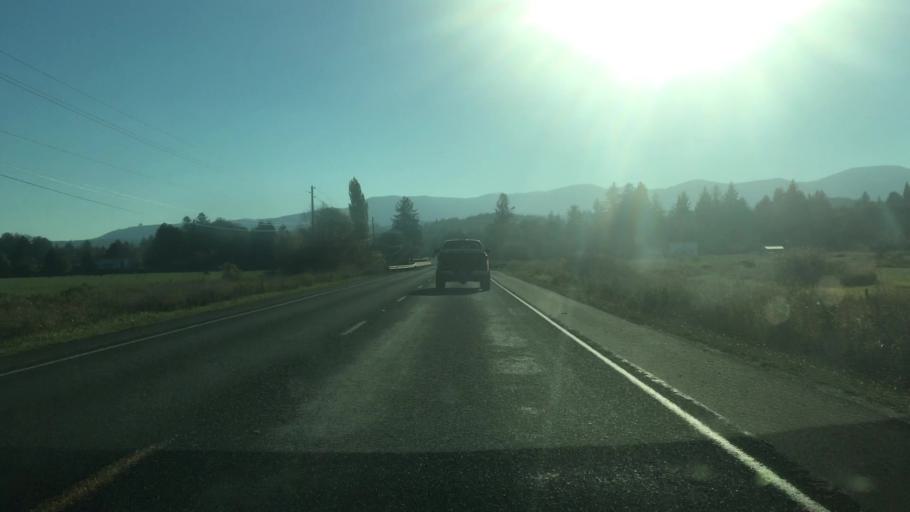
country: US
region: Oregon
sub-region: Clatsop County
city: Astoria
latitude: 46.3706
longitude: -123.8068
